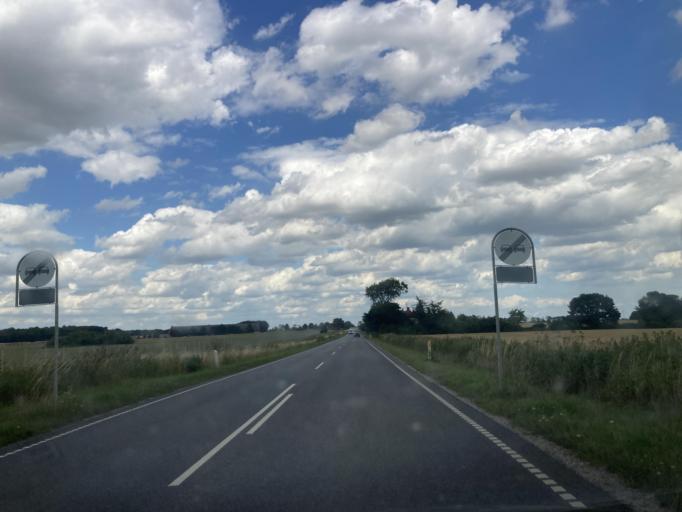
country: DK
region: Zealand
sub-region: Faxe Kommune
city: Haslev
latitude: 55.3314
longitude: 12.0193
